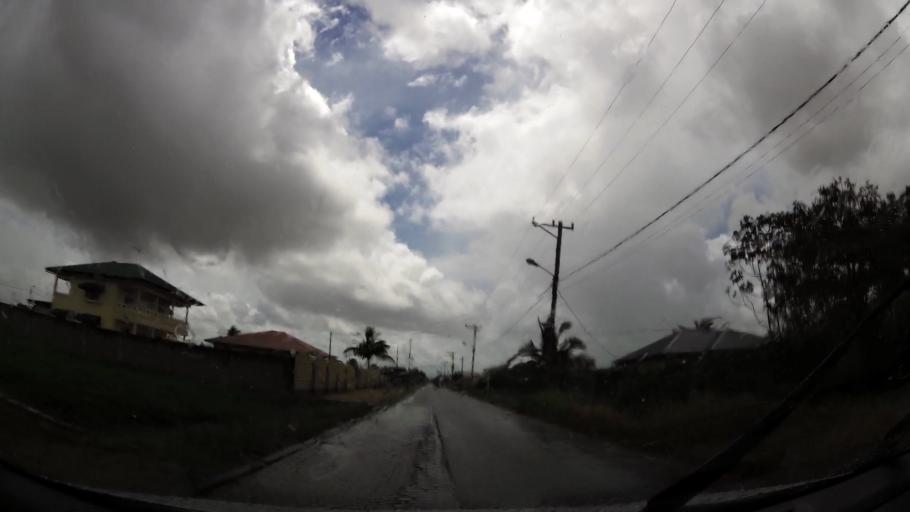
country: SR
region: Paramaribo
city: Paramaribo
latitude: 5.8290
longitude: -55.2341
